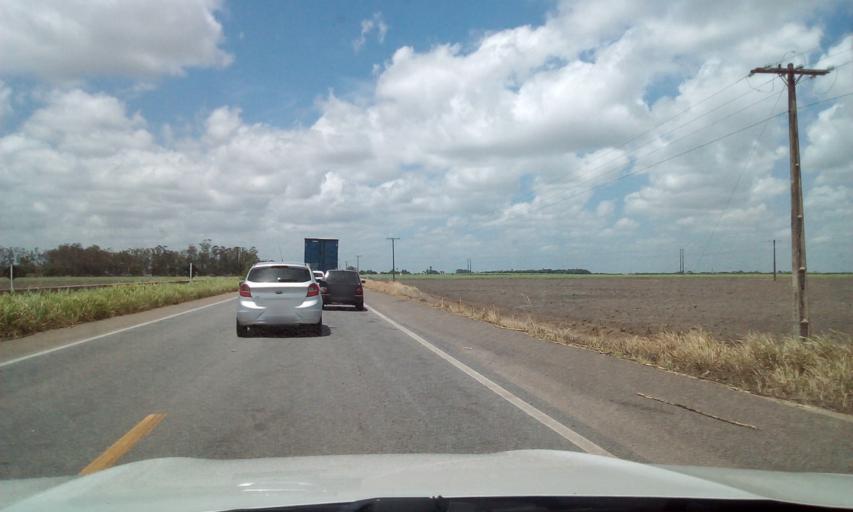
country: BR
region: Alagoas
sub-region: Campo Alegre
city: Campo Alegre
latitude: -9.9032
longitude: -36.2291
